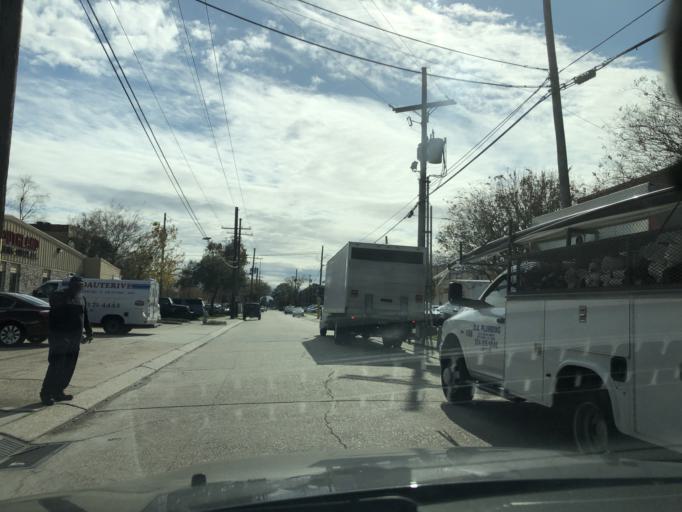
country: US
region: Louisiana
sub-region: Jefferson Parish
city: Metairie
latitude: 29.9956
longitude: -90.1609
